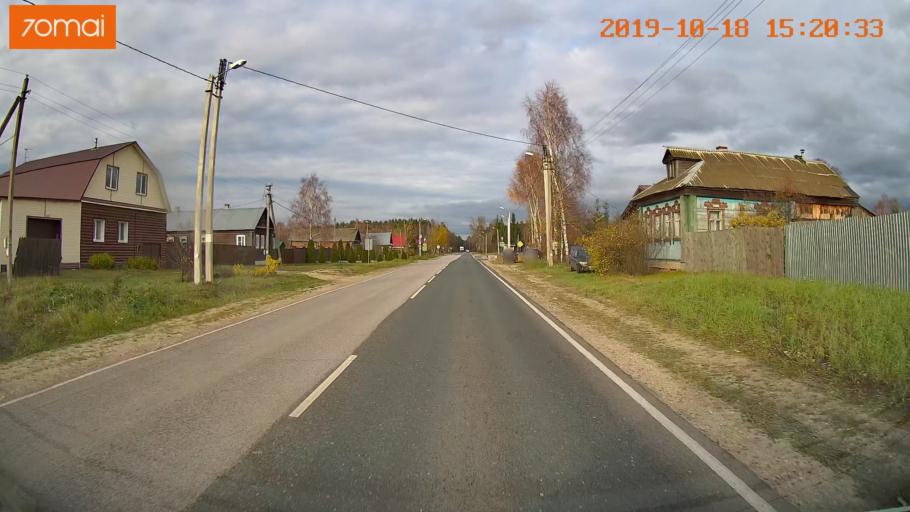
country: RU
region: Vladimir
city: Anopino
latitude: 55.6881
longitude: 40.7454
